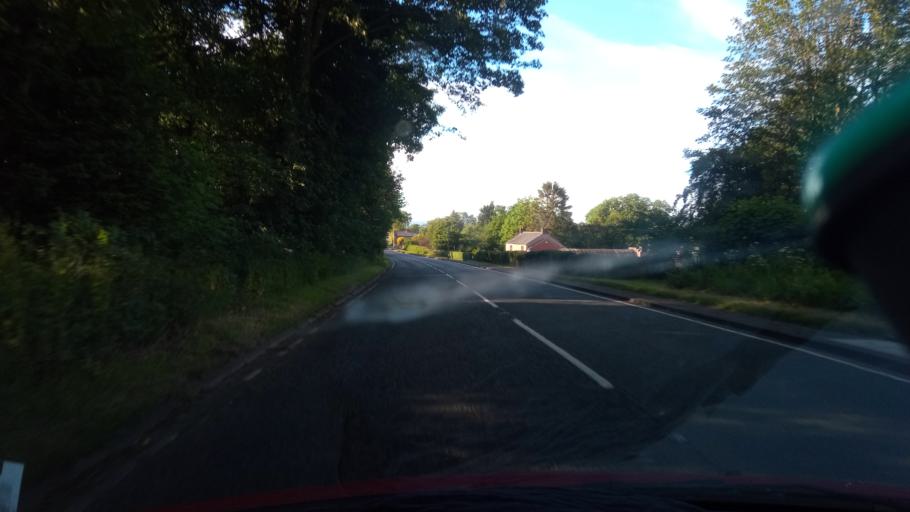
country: GB
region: England
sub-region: Cumbria
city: Carlisle
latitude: 54.9440
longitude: -2.9436
